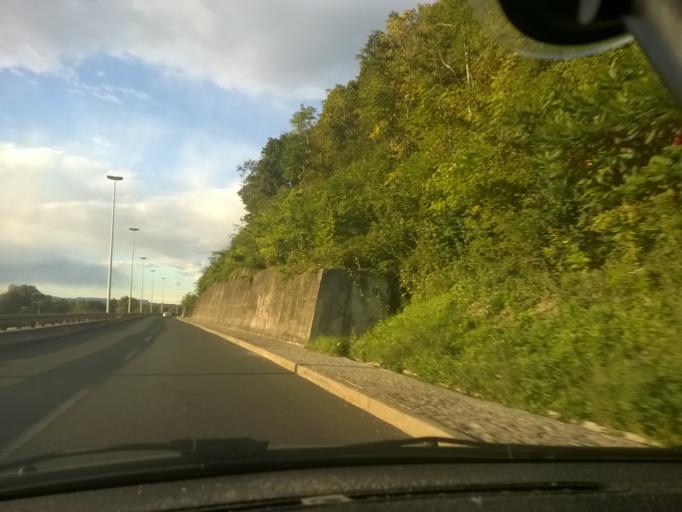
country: HR
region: Zagrebacka
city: Bestovje
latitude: 45.8284
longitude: 15.8251
